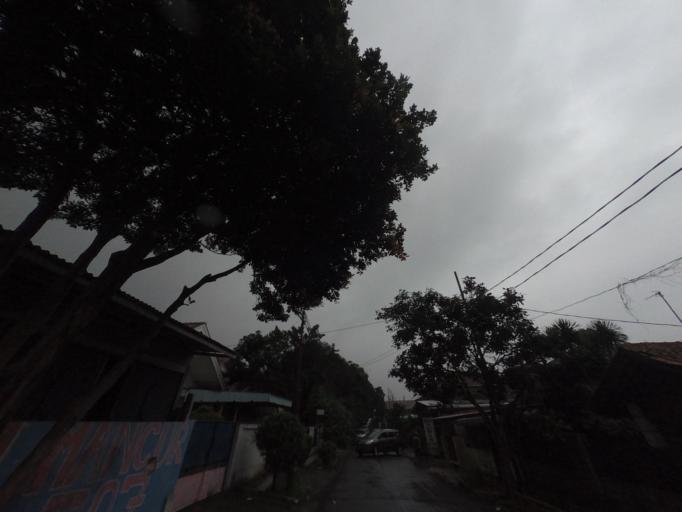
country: ID
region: West Java
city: Bogor
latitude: -6.5713
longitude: 106.7932
